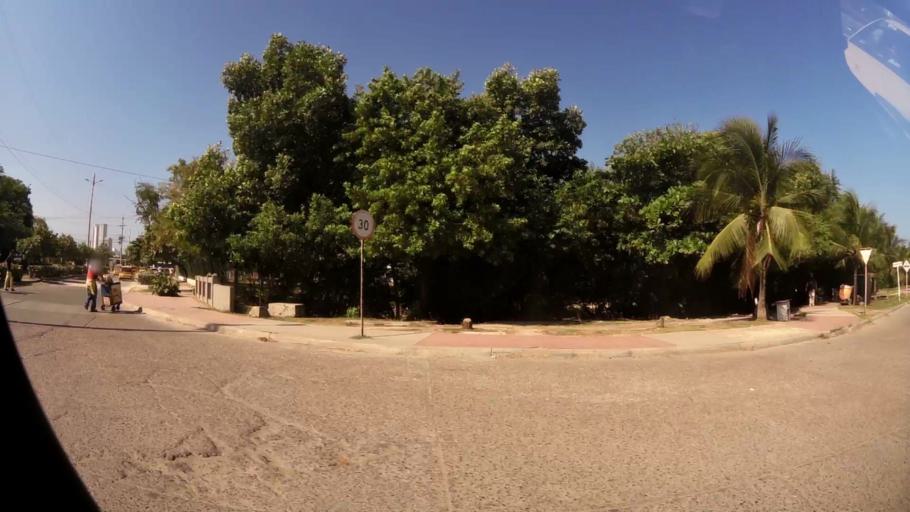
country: CO
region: Bolivar
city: Cartagena
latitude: 10.4274
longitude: -75.5406
